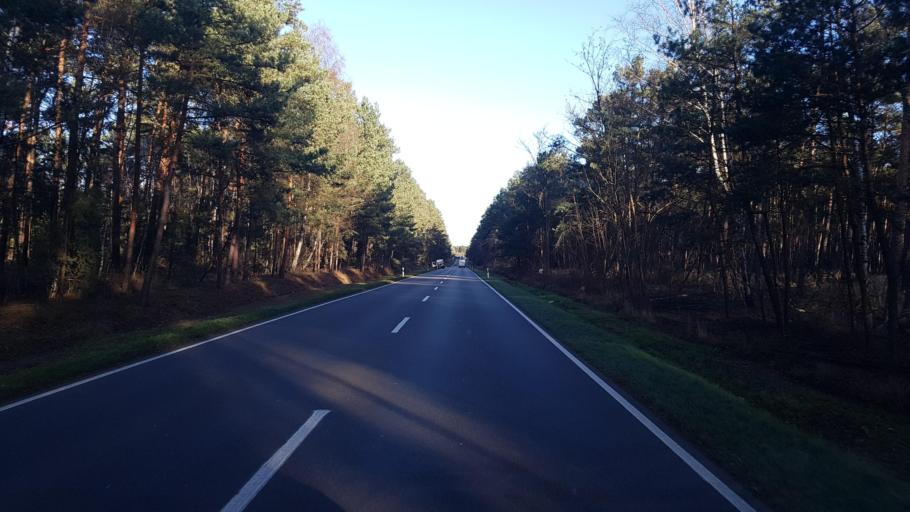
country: DE
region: Brandenburg
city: Heinersbruck
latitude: 51.7192
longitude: 14.4584
